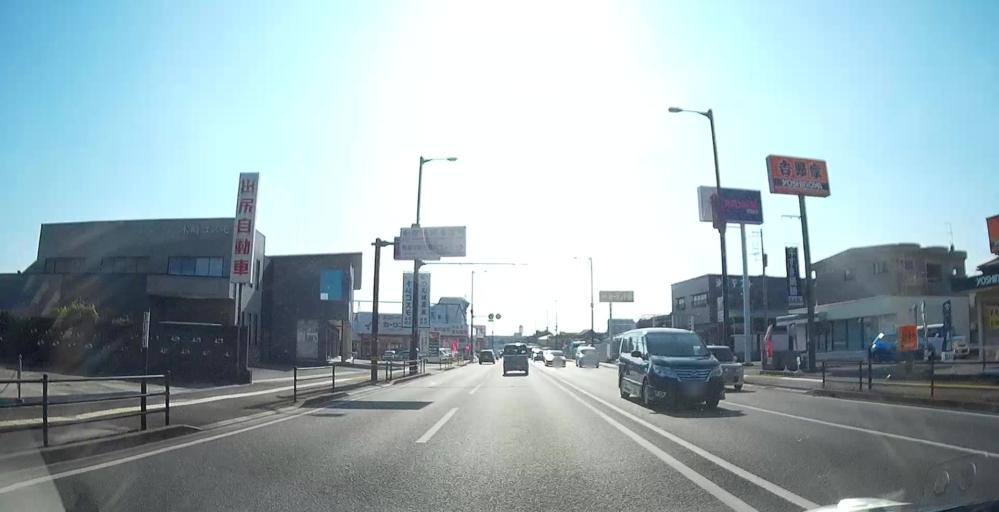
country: JP
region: Kumamoto
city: Kumamoto
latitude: 32.7653
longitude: 130.6908
